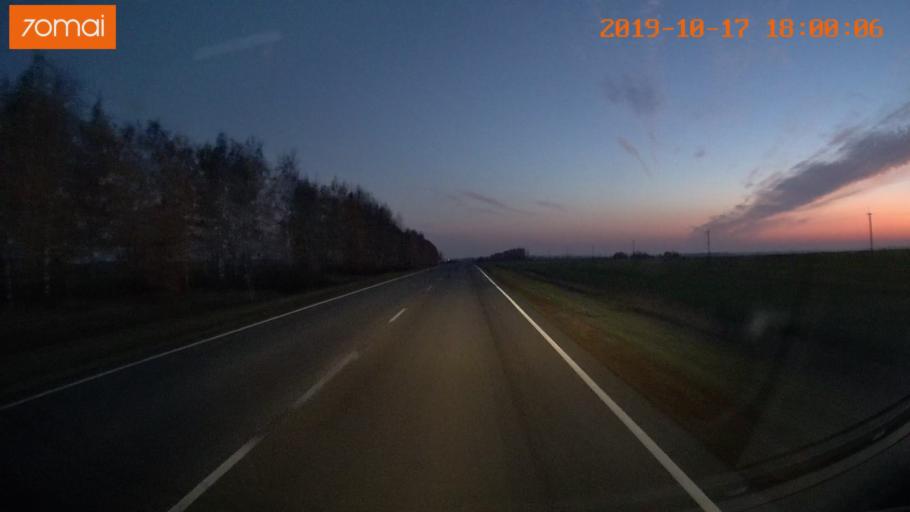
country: RU
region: Tula
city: Kurkino
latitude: 53.5273
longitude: 38.6174
